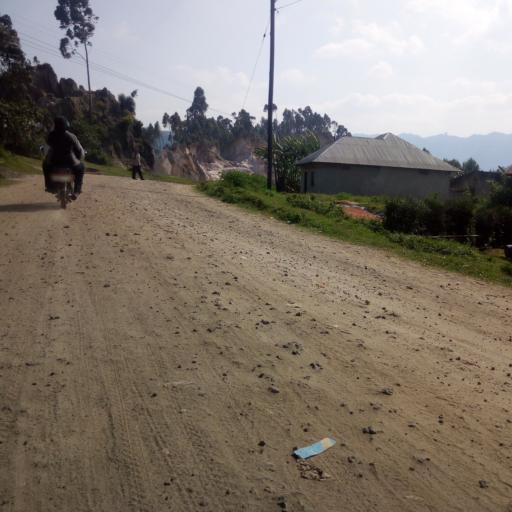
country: UG
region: Western Region
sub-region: Kisoro District
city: Kisoro
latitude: -1.2299
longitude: 29.7108
